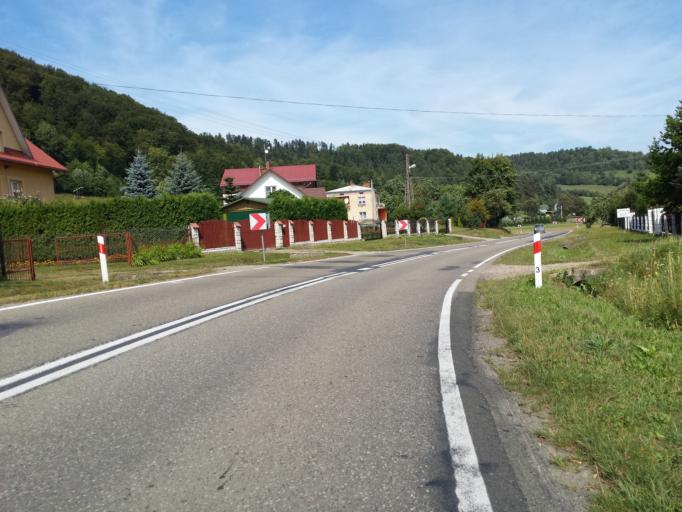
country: PL
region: Subcarpathian Voivodeship
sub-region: Powiat leski
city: Baligrod
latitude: 49.3942
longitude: 22.2810
